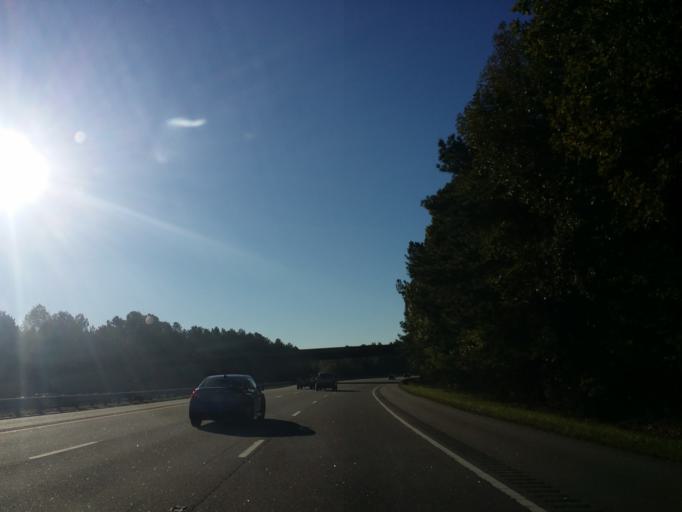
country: US
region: North Carolina
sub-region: Wake County
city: Cary
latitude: 35.8179
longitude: -78.7401
